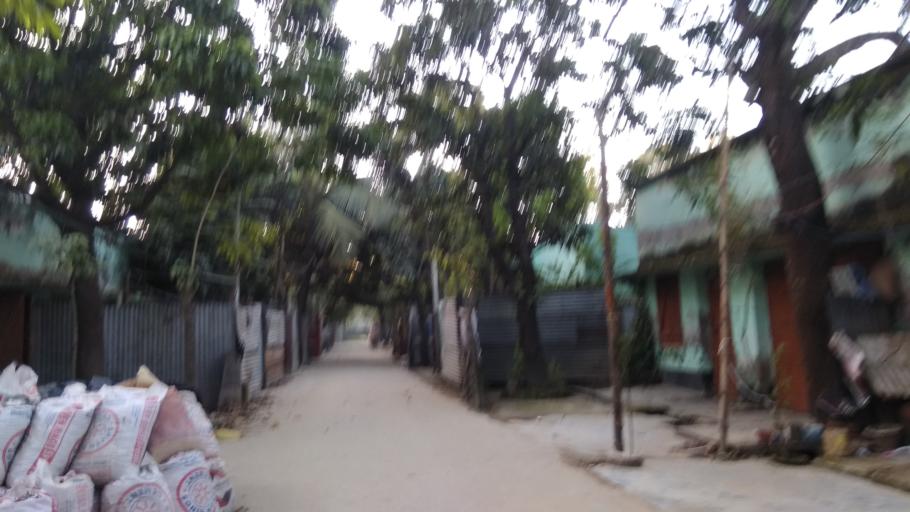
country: BD
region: Dhaka
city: Tungi
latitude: 23.8438
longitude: 90.4212
